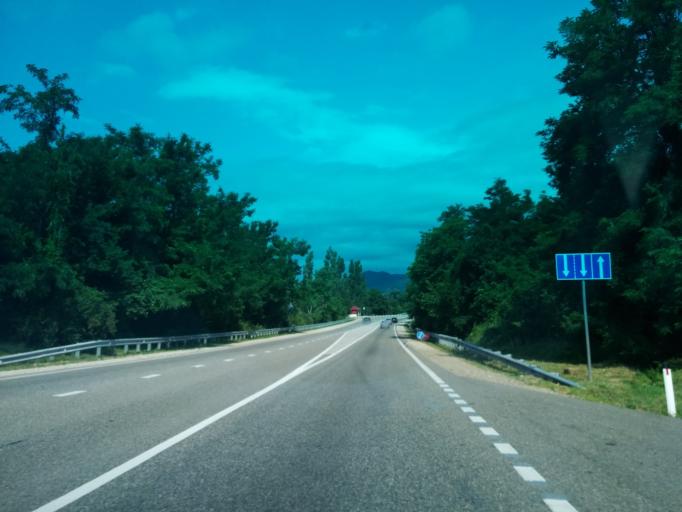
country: RU
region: Krasnodarskiy
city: Nebug
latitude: 44.1545
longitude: 39.0078
